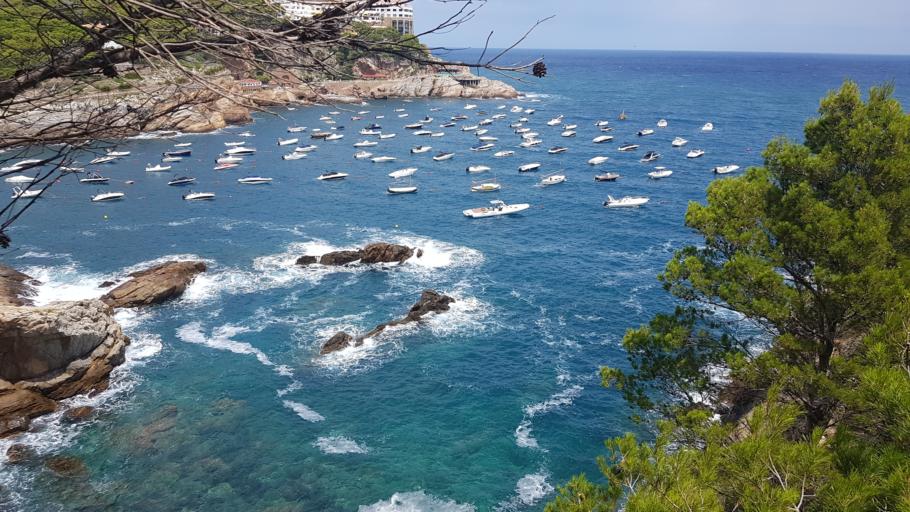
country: ES
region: Catalonia
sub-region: Provincia de Girona
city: Begur
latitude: 41.9622
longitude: 3.2292
